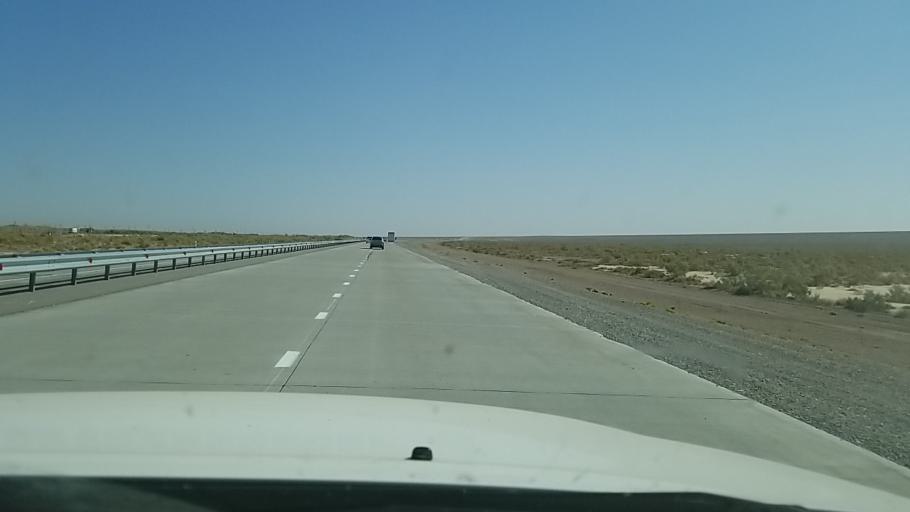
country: KZ
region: Almaty Oblysy
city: Kegen
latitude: 43.7543
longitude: 78.9155
